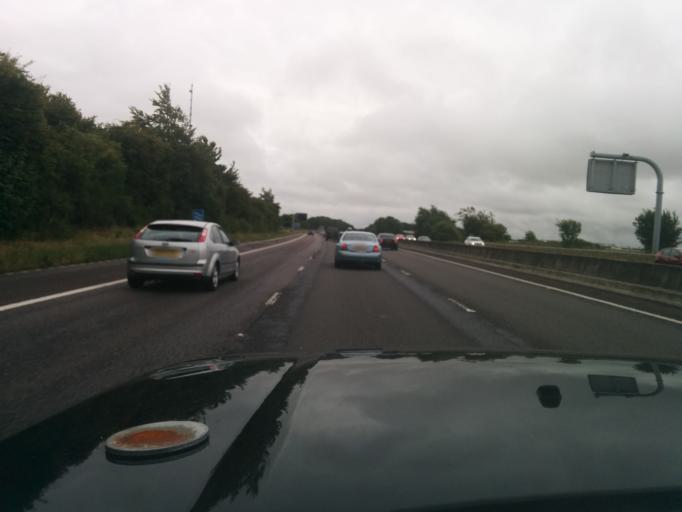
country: GB
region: England
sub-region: West Berkshire
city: Lambourn
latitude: 51.4862
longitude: -1.5689
